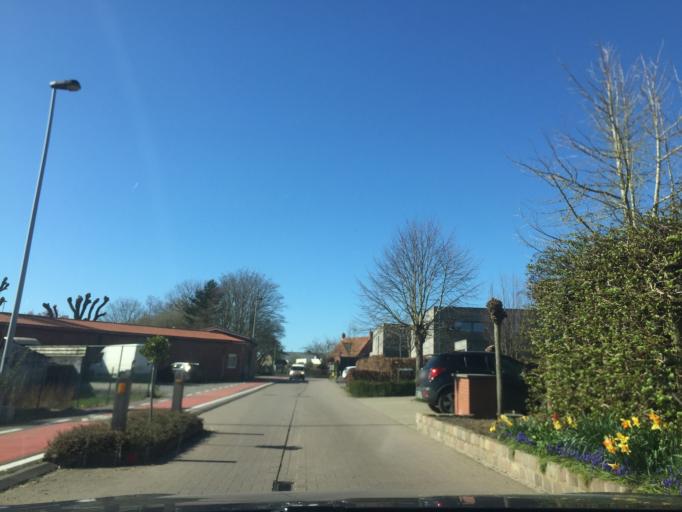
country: BE
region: Flanders
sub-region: Provincie West-Vlaanderen
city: Hooglede
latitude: 50.9749
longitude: 3.0751
